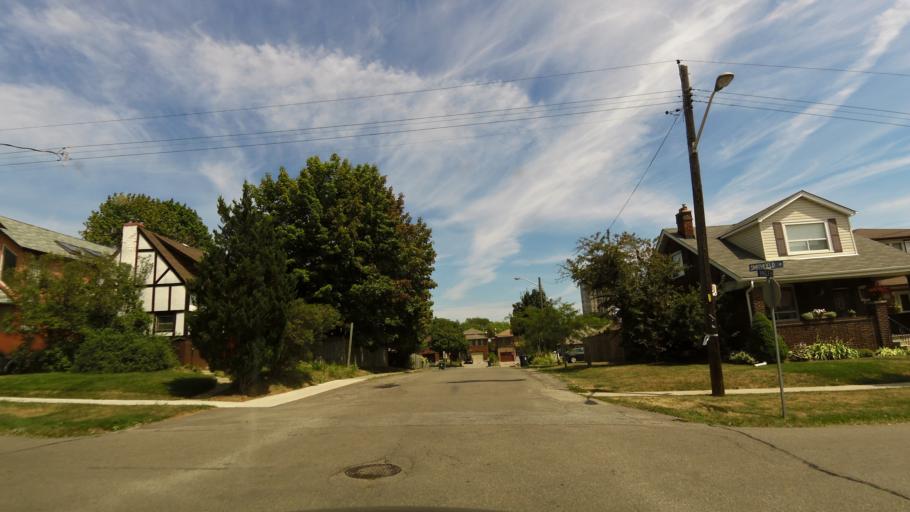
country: CA
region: Ontario
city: Etobicoke
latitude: 43.6311
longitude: -79.4858
